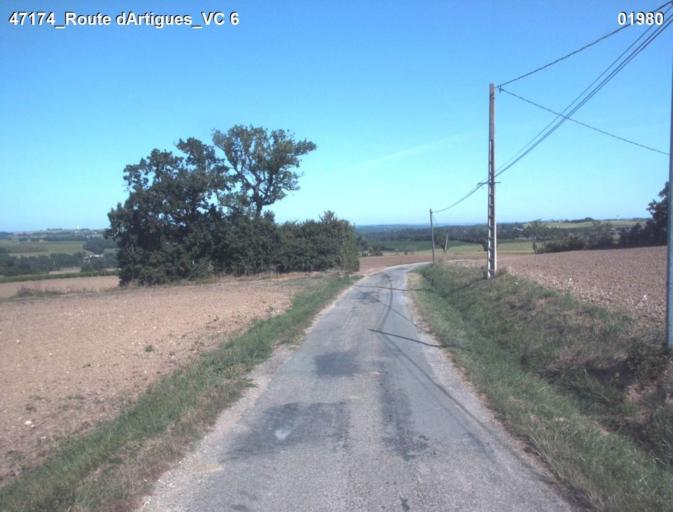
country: FR
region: Midi-Pyrenees
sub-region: Departement du Gers
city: Condom
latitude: 44.0245
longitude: 0.3334
